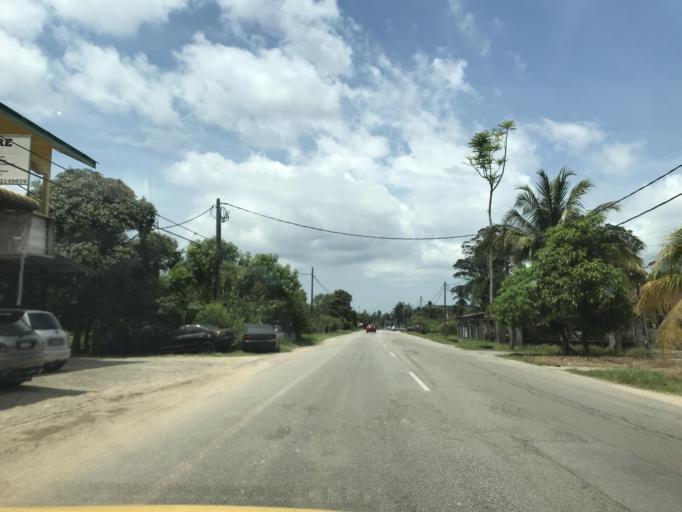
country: MY
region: Kelantan
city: Pasir Mas
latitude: 6.0507
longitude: 102.1833
